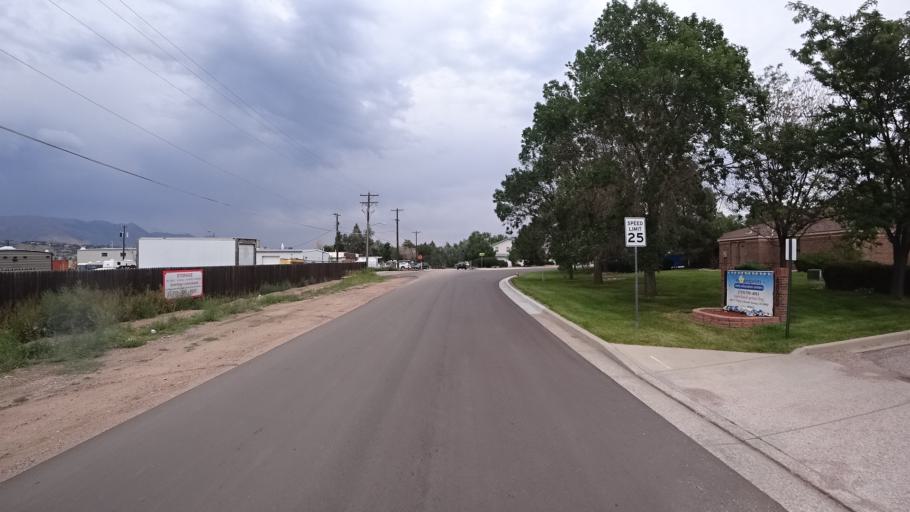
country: US
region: Colorado
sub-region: El Paso County
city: Colorado Springs
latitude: 38.8916
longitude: -104.8154
